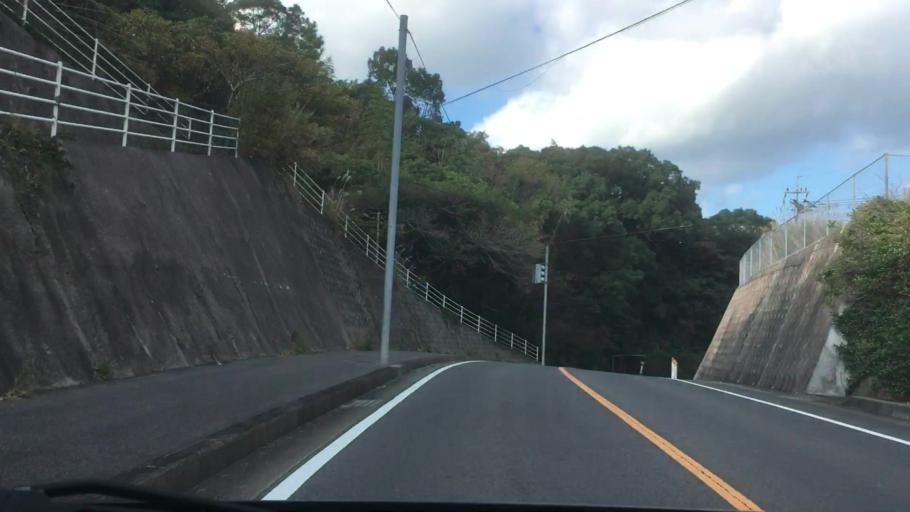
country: JP
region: Nagasaki
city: Sasebo
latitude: 33.0344
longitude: 129.6111
